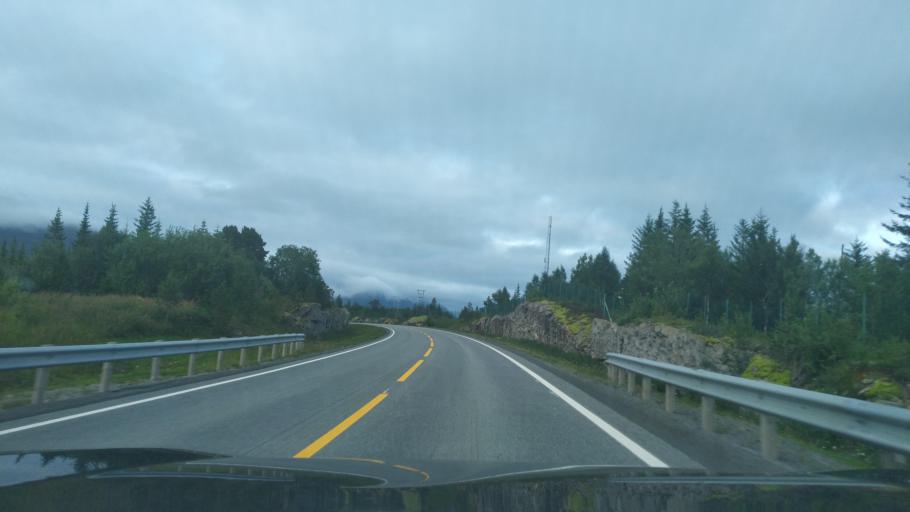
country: NO
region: Nordland
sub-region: Narvik
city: Narvik
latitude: 68.5224
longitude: 17.3891
